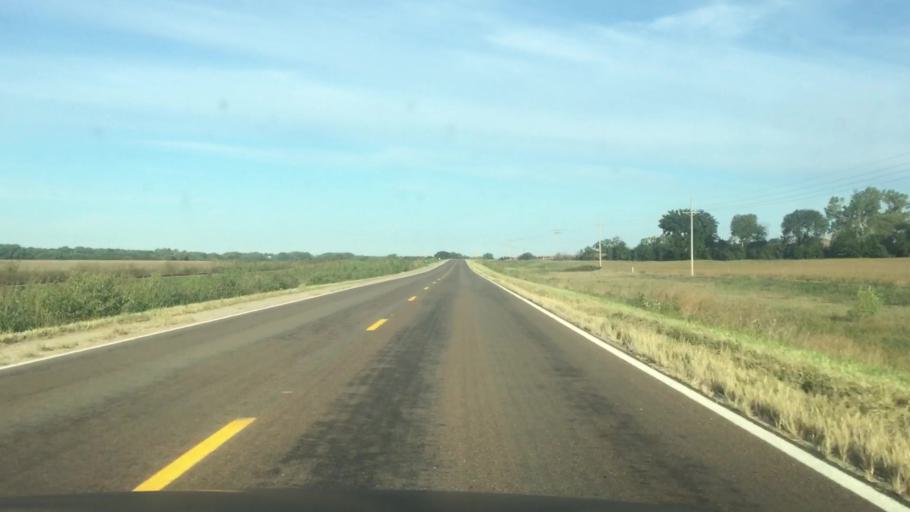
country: US
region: Nebraska
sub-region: Jefferson County
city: Fairbury
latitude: 40.0833
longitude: -97.1097
